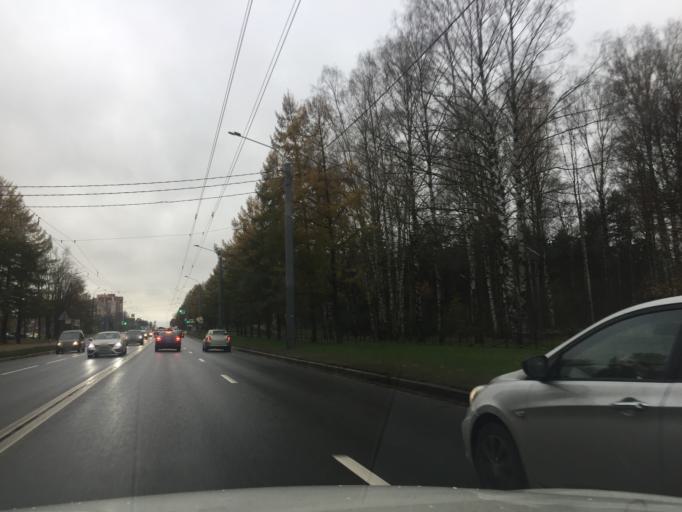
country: RU
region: St.-Petersburg
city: Sosnovka
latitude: 60.0162
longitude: 30.3607
